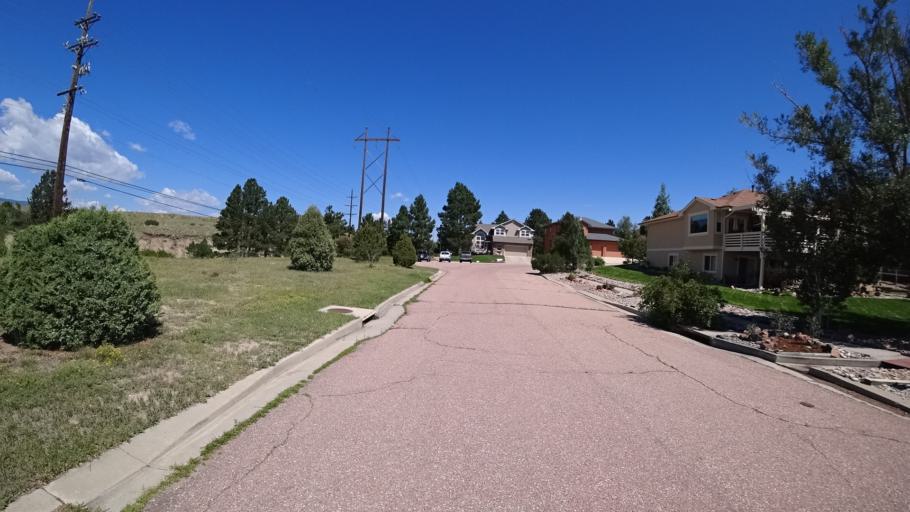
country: US
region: Colorado
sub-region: El Paso County
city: Gleneagle
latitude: 38.9827
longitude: -104.7828
